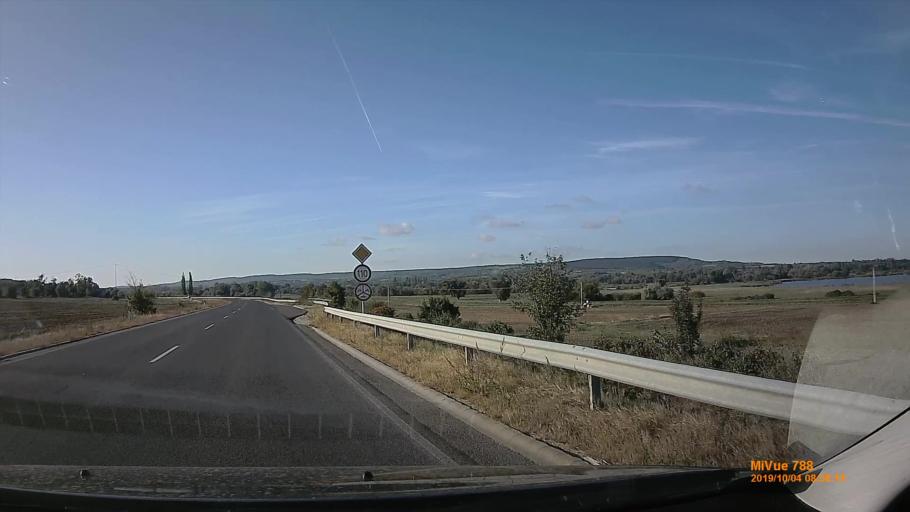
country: HU
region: Somogy
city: Balatonlelle
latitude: 46.7763
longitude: 17.7579
